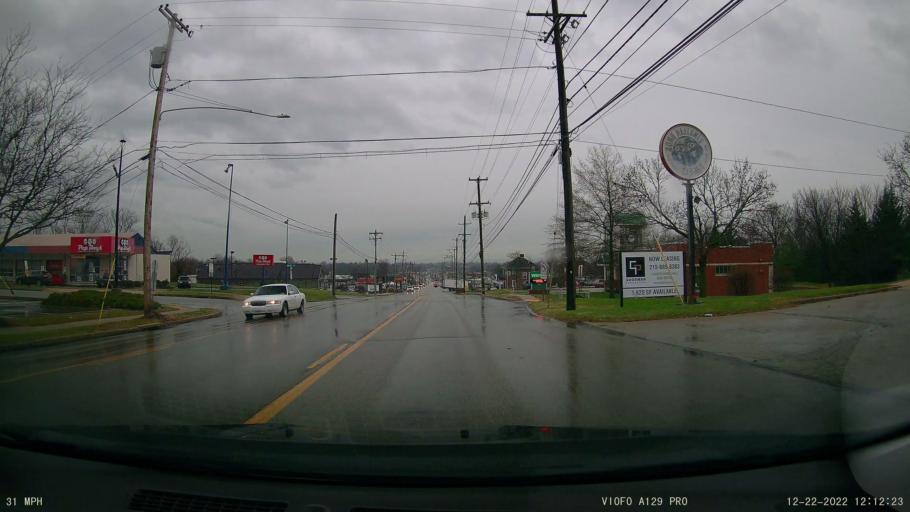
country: US
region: Pennsylvania
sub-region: Montgomery County
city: Trooper
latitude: 40.1455
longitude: -75.3941
